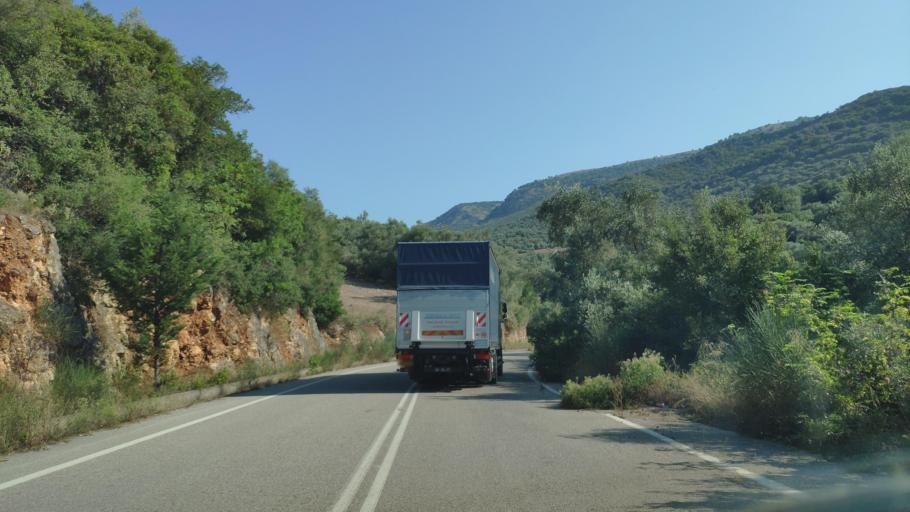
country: GR
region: West Greece
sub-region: Nomos Aitolias kai Akarnanias
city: Stanos
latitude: 38.7754
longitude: 21.1481
